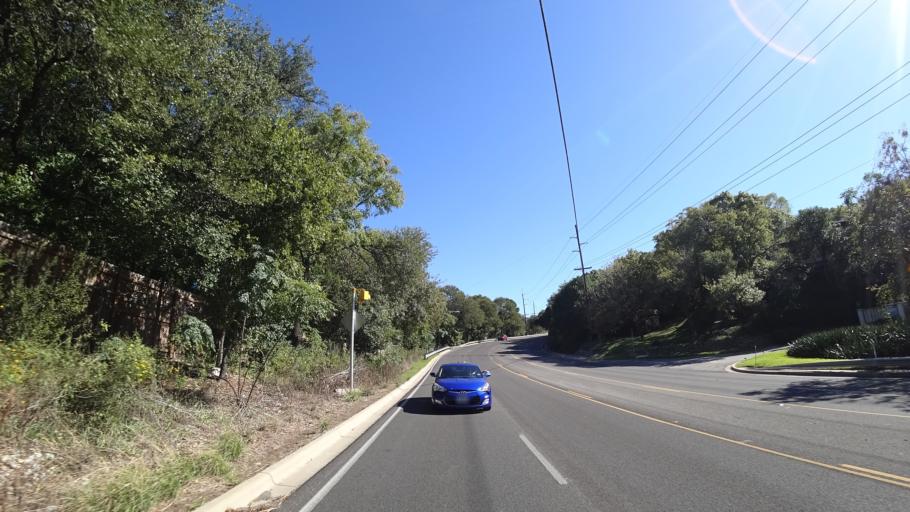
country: US
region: Texas
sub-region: Travis County
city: West Lake Hills
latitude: 30.3416
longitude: -97.7609
